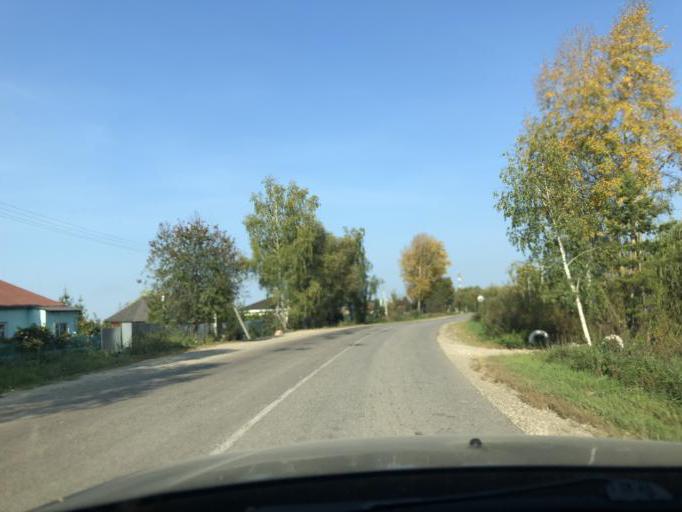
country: RU
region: Tula
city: Leninskiy
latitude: 54.3406
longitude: 37.3692
